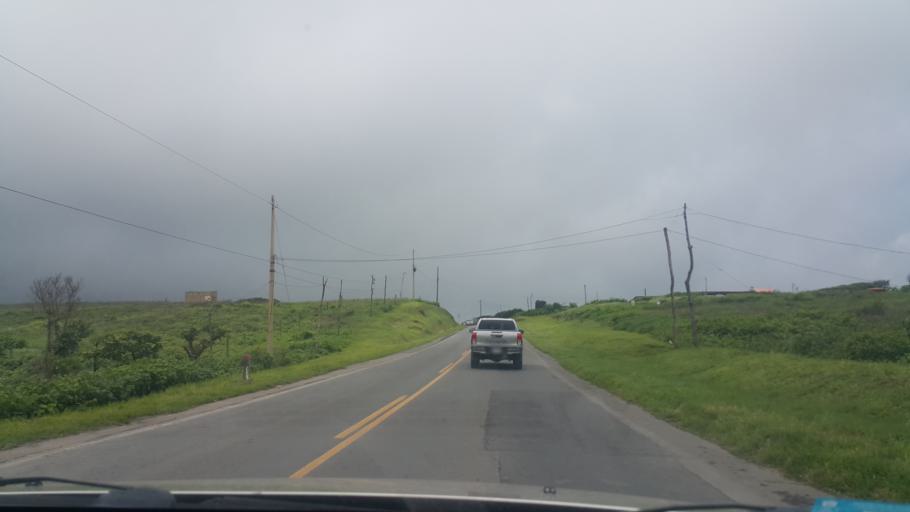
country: NI
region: Managua
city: El Crucero
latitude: 11.9410
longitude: -86.2971
